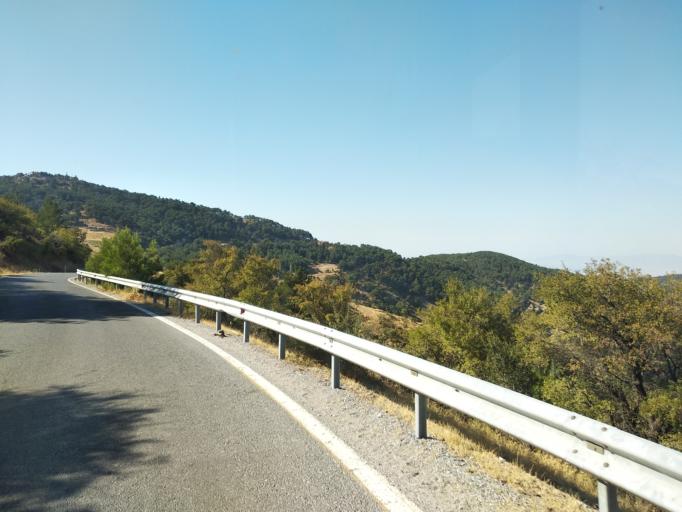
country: TR
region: Izmir
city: Gaziemir
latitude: 38.3240
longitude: 27.0071
